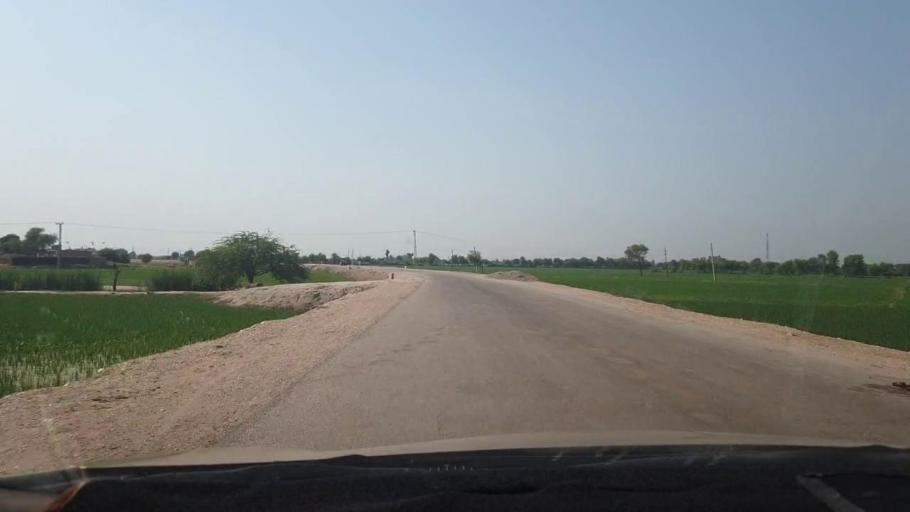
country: PK
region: Sindh
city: Larkana
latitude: 27.6090
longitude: 68.2386
